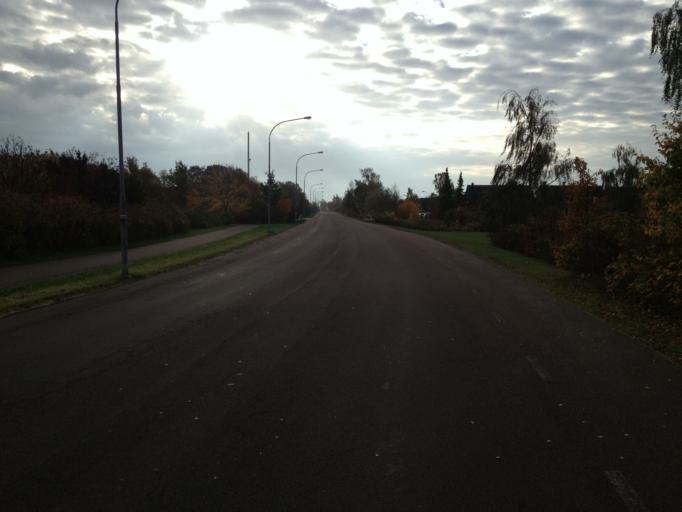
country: SE
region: Skane
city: Bjarred
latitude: 55.7290
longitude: 13.0076
